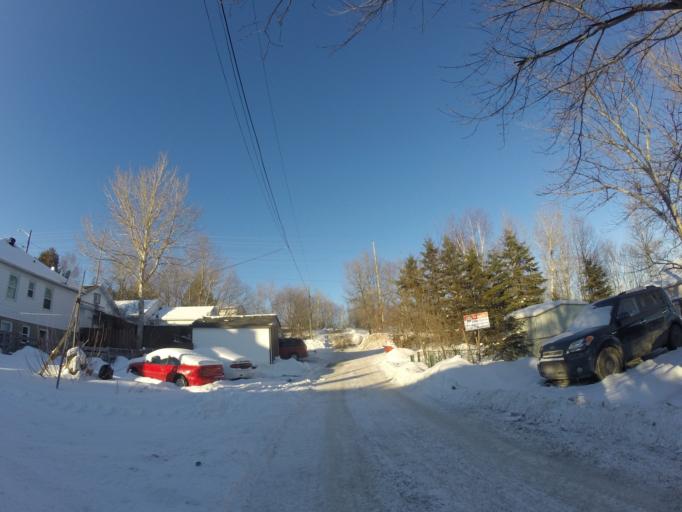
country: CA
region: Ontario
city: Greater Sudbury
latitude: 46.5037
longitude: -81.0000
